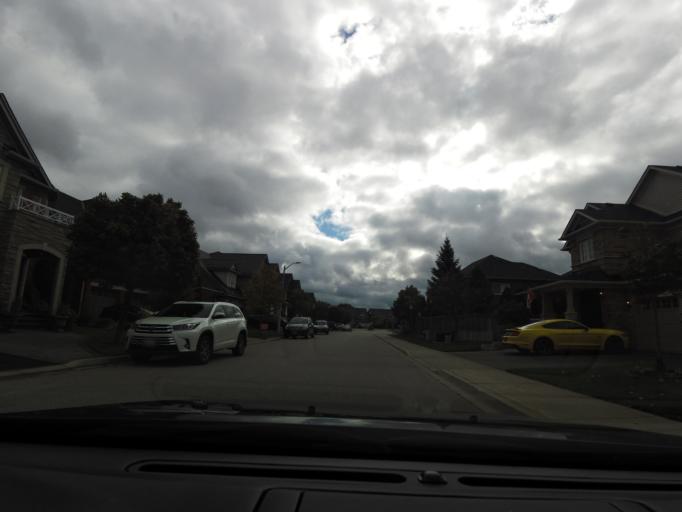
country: CA
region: Ontario
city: Burlington
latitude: 43.4044
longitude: -79.7875
